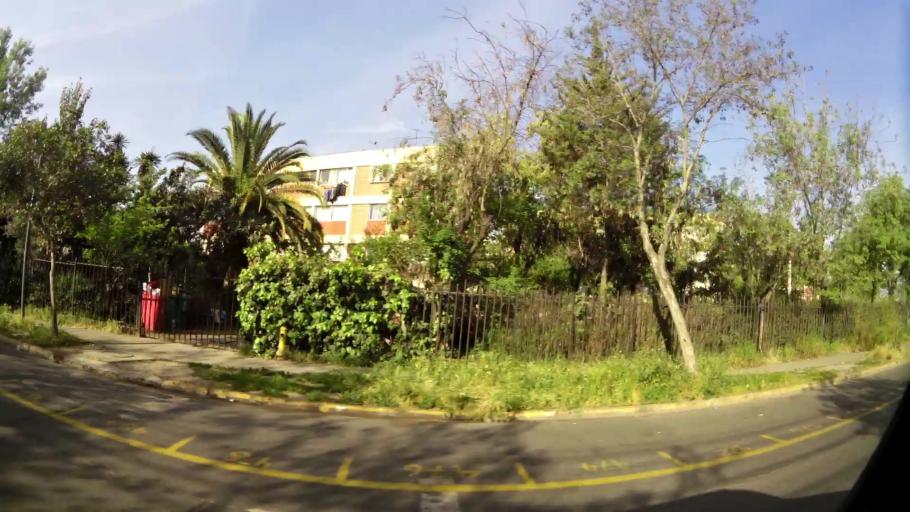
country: CL
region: Santiago Metropolitan
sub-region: Provincia de Santiago
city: Santiago
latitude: -33.5082
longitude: -70.6238
